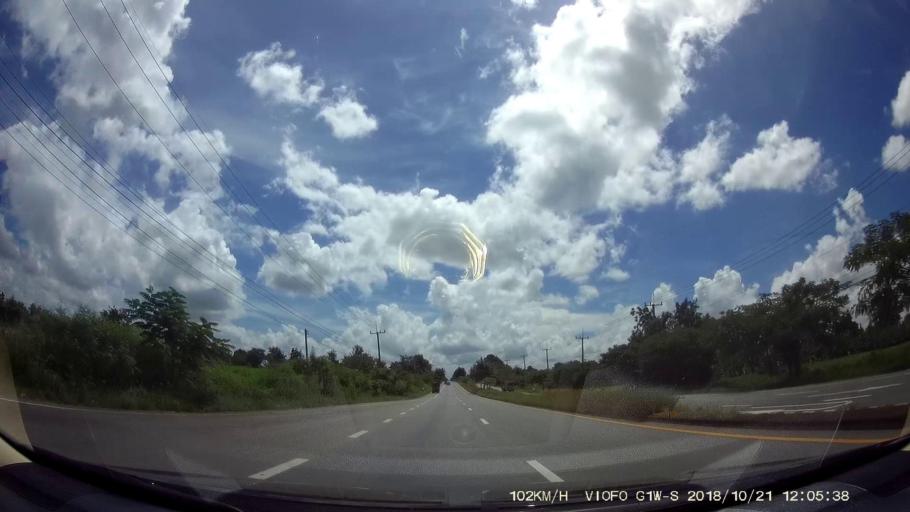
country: TH
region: Chaiyaphum
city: Chatturat
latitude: 15.4758
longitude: 101.8240
